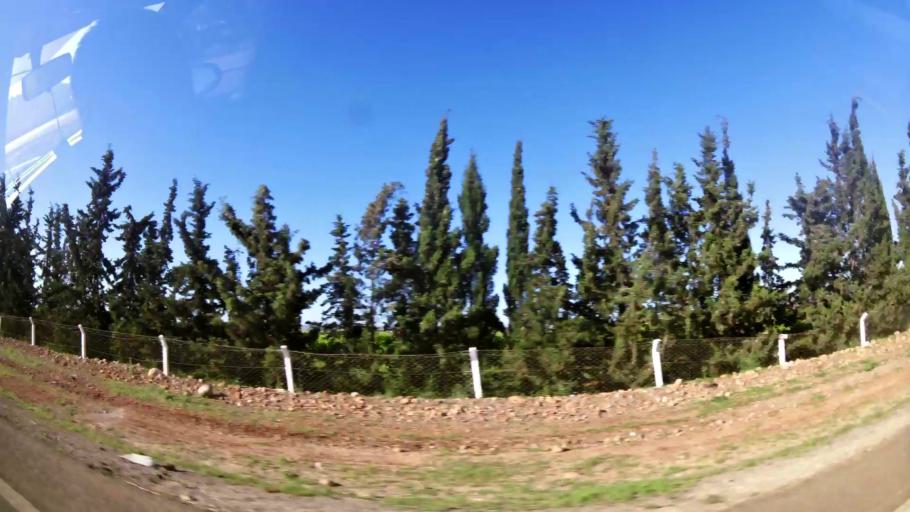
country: MA
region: Oriental
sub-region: Berkane-Taourirt
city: Ahfir
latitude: 35.0027
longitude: -2.1795
